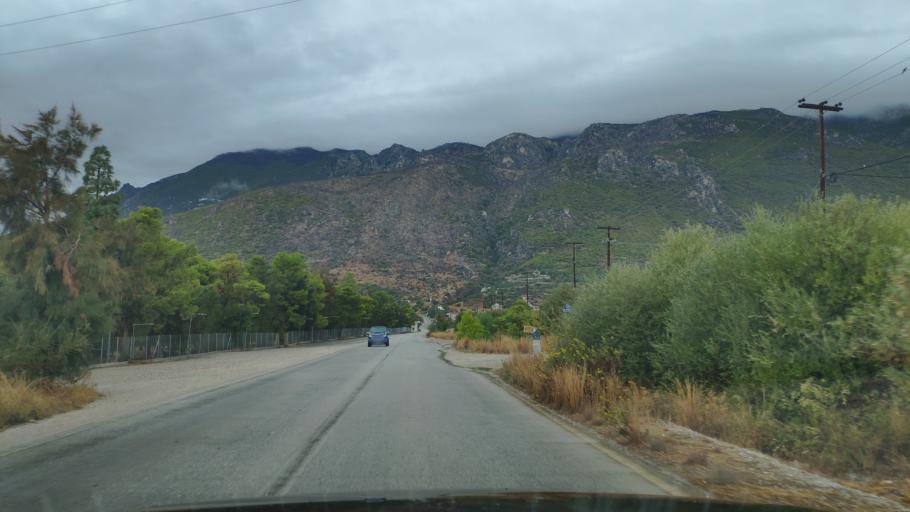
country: GR
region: Peloponnese
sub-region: Nomos Korinthias
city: Loutraki
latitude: 37.9706
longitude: 22.9875
